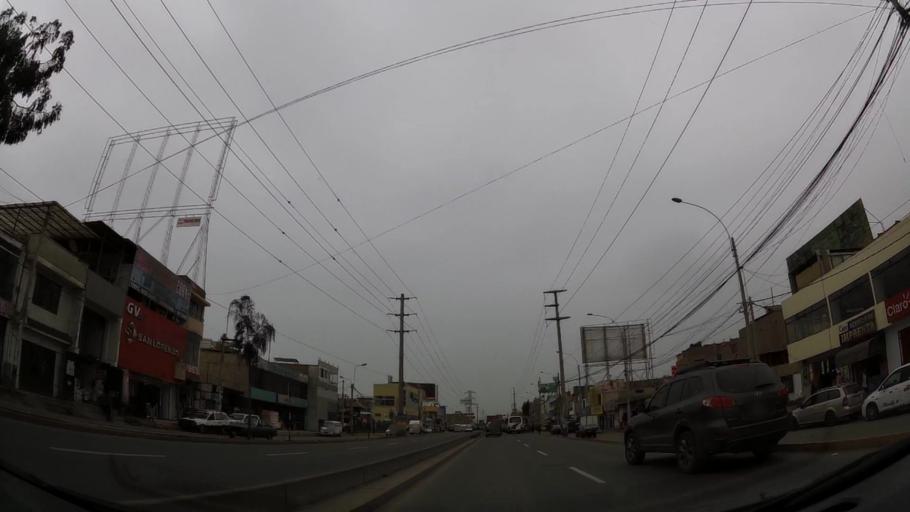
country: PE
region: Lima
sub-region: Lima
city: Punta Hermosa
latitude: -12.2781
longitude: -76.8689
